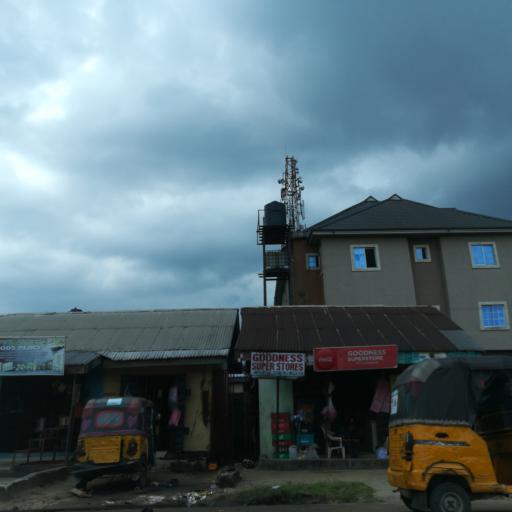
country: NG
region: Rivers
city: Port Harcourt
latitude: 4.8139
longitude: 7.0594
